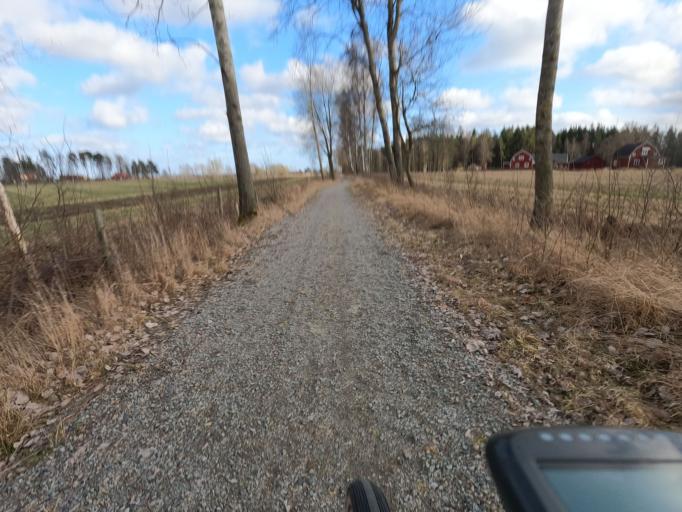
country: SE
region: Kronoberg
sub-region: Alvesta Kommun
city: Vislanda
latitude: 56.7259
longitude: 14.5700
